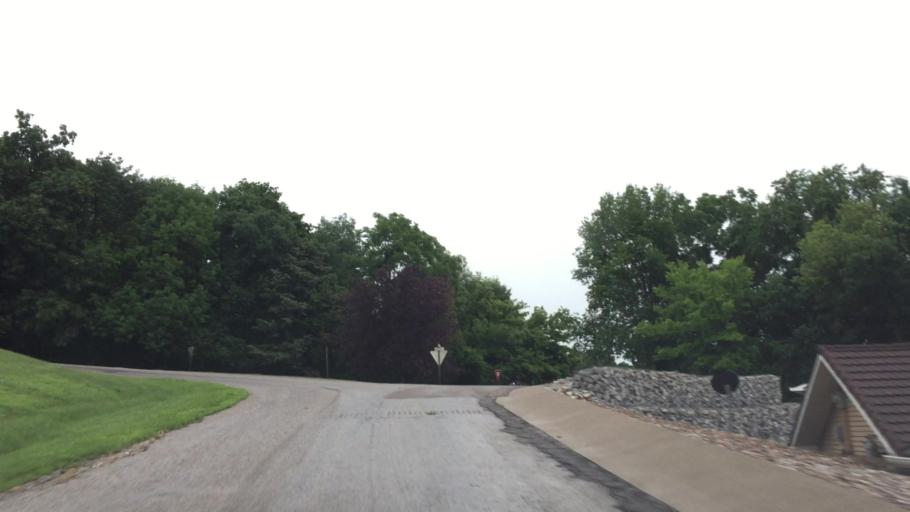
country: US
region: Illinois
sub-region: Hancock County
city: Nauvoo
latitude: 40.5303
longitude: -91.3722
